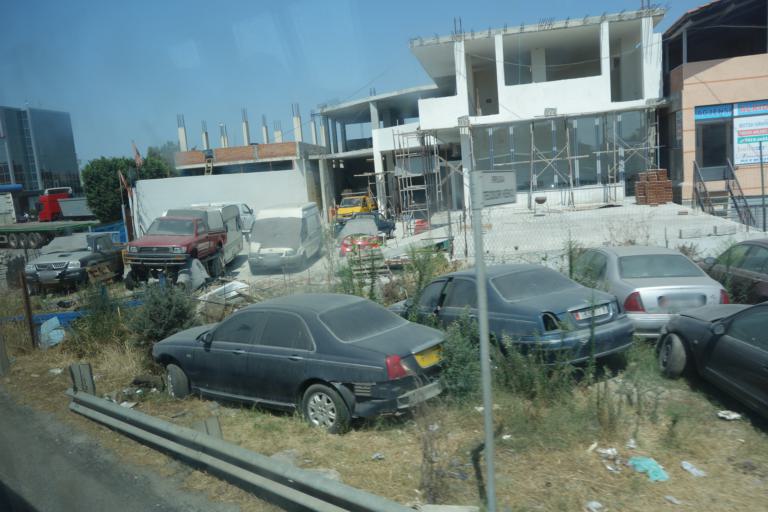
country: AL
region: Durres
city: Durres
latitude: 41.3207
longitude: 19.4705
